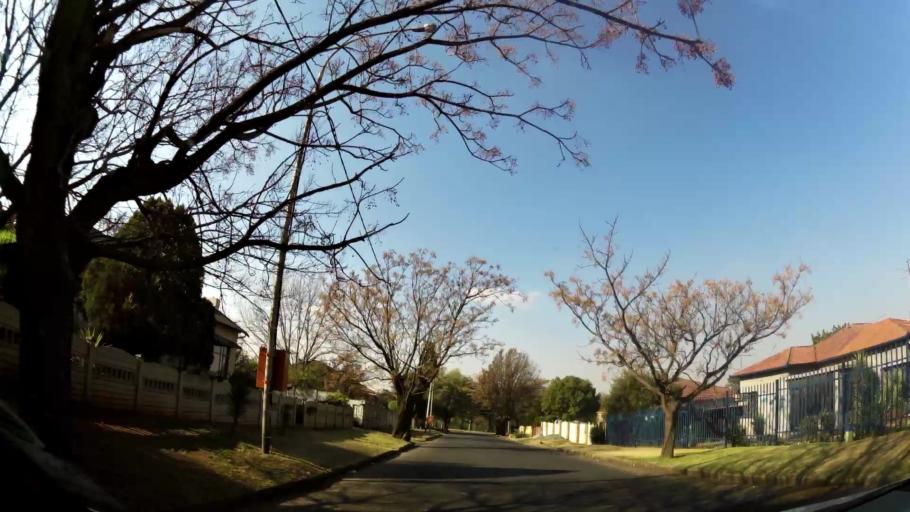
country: ZA
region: Gauteng
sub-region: Ekurhuleni Metropolitan Municipality
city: Brakpan
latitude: -26.2258
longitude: 28.3622
